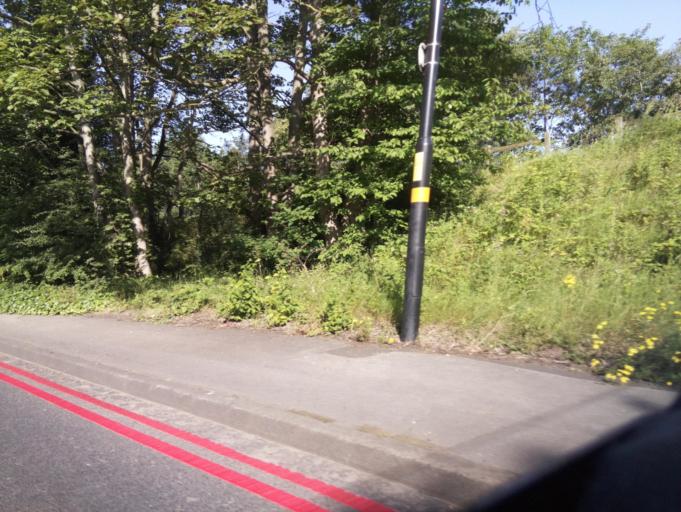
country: GB
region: England
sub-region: City and Borough of Birmingham
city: Sutton Coldfield
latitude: 52.5257
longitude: -1.7890
